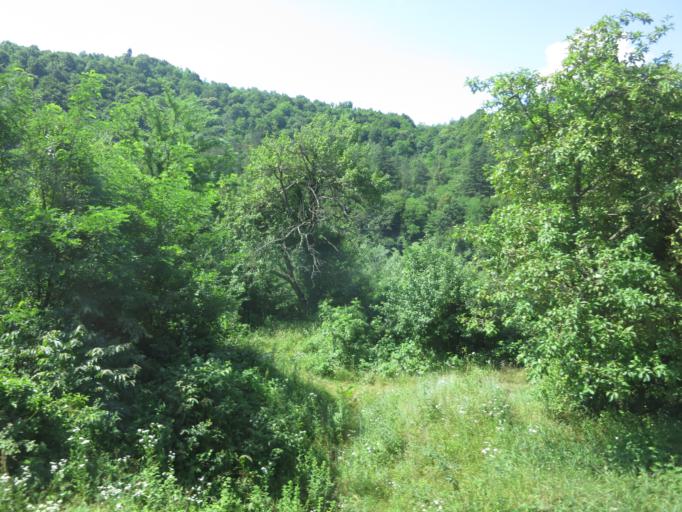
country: GE
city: Shorapani
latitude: 42.0956
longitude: 43.1133
